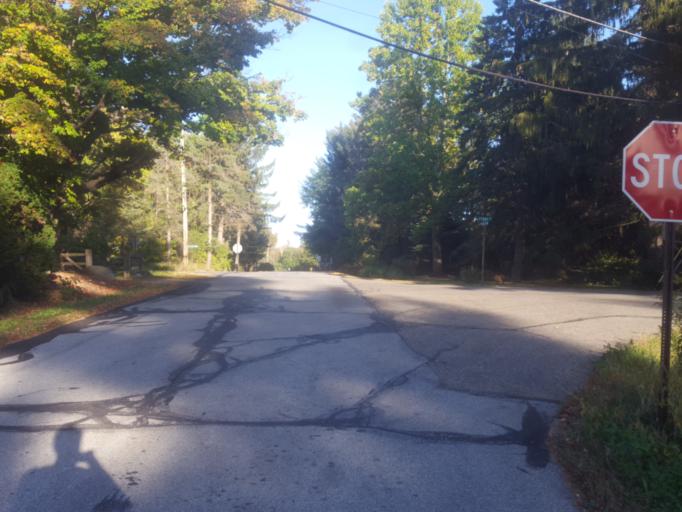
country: US
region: Ohio
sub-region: Cuyahoga County
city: Gates Mills
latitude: 41.5626
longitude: -81.3817
